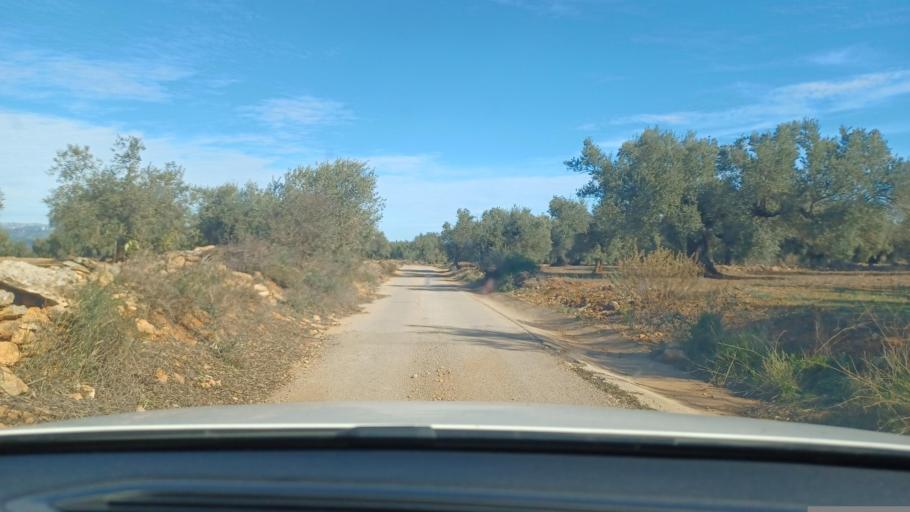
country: ES
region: Catalonia
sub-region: Provincia de Tarragona
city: Santa Barbara
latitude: 40.6895
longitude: 0.5043
